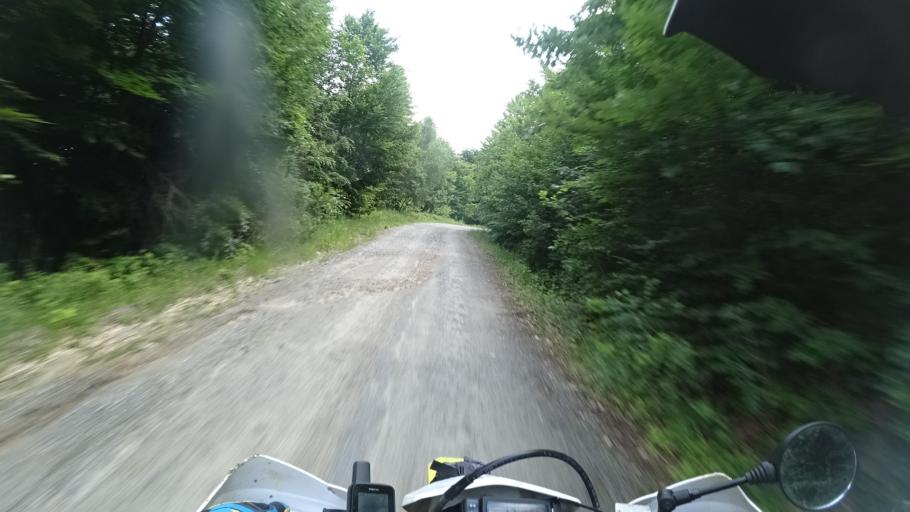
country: HR
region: Sisacko-Moslavacka
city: Gvozd
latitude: 45.3144
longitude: 15.8089
